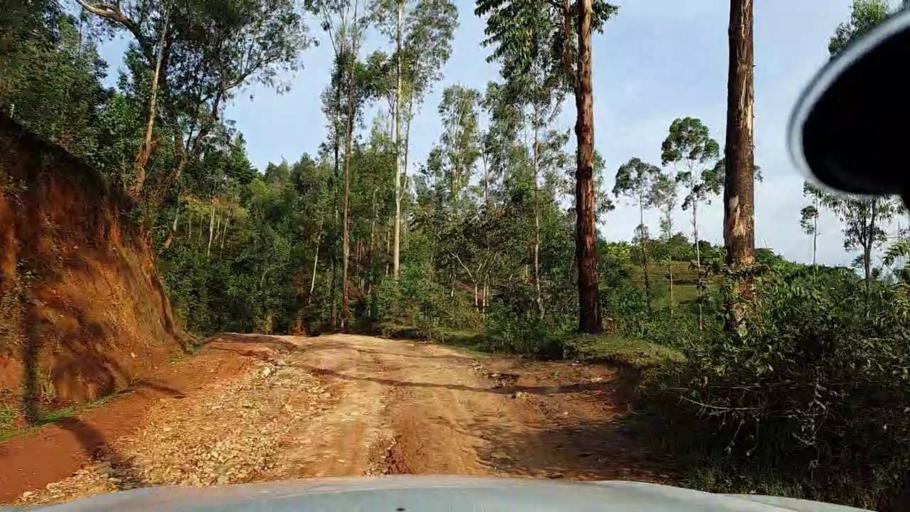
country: RW
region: Southern Province
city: Gitarama
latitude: -2.1728
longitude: 29.5551
